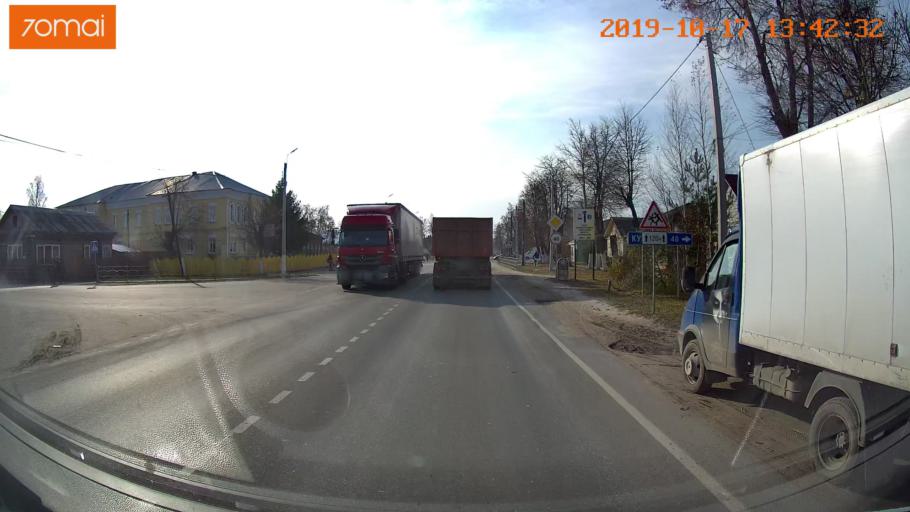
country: RU
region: Rjazan
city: Tuma
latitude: 55.1468
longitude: 40.5526
